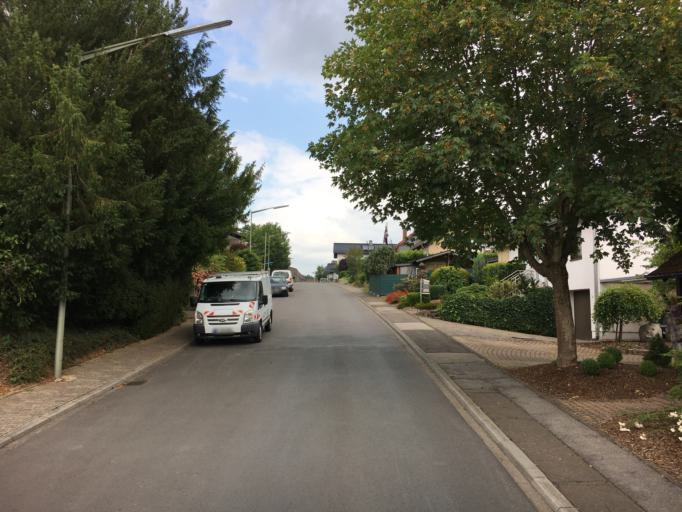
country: DE
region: North Rhine-Westphalia
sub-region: Regierungsbezirk Arnsberg
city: Lennestadt
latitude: 51.1213
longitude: 8.0579
